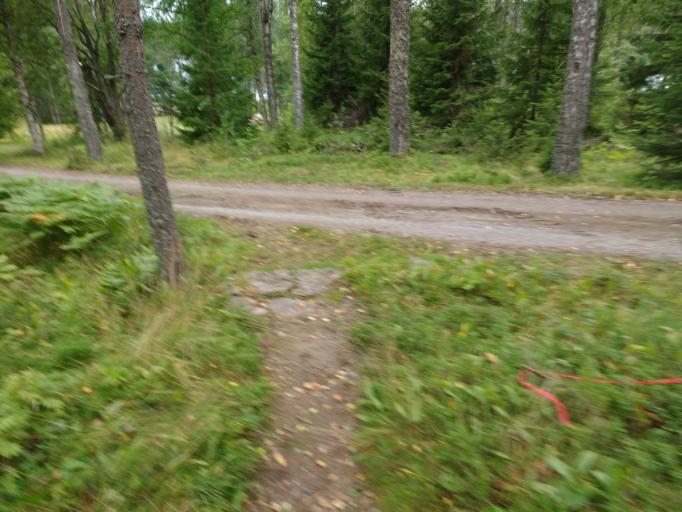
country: FI
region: Pirkanmaa
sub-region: Ylae-Pirkanmaa
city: Juupajoki
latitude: 61.8471
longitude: 24.2857
